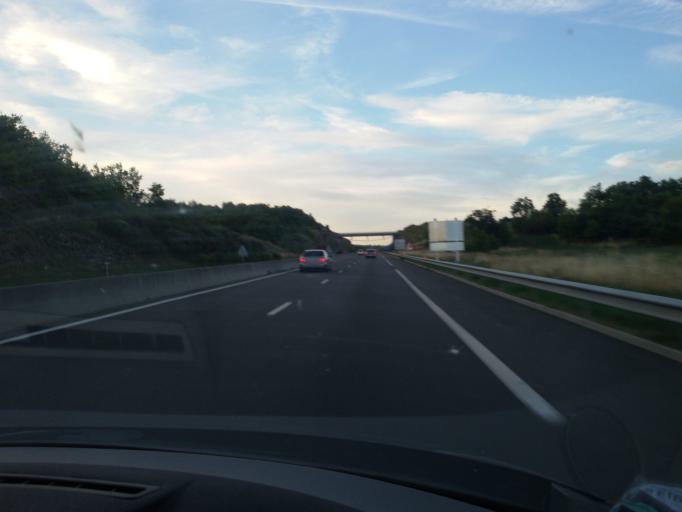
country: FR
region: Languedoc-Roussillon
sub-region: Departement de la Lozere
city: Chirac
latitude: 44.5165
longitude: 3.2411
